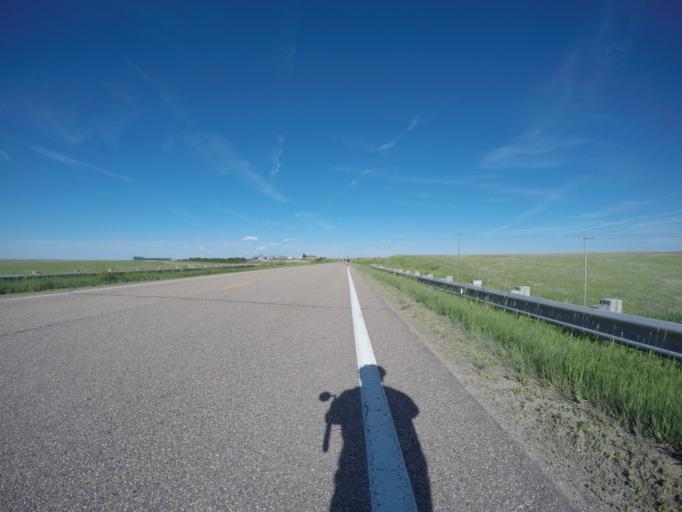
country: US
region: Kansas
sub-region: Cheyenne County
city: Saint Francis
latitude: 39.7565
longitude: -102.0192
